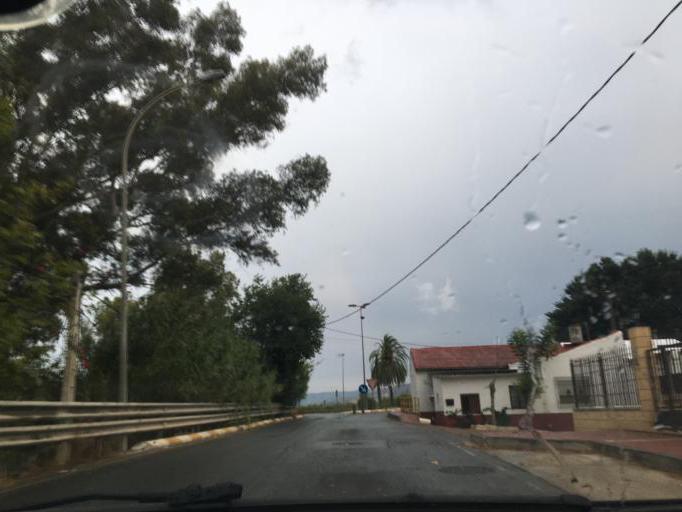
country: ES
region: Murcia
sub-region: Murcia
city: Santomera
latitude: 38.0242
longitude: -1.0454
